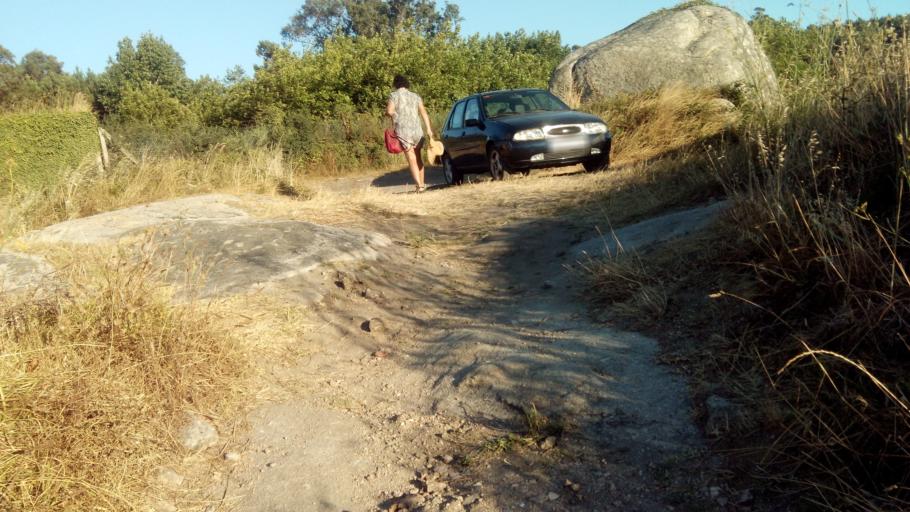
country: ES
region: Galicia
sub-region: Provincia de Pontevedra
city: Vilanova de Arousa
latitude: 42.5720
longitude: -8.8839
